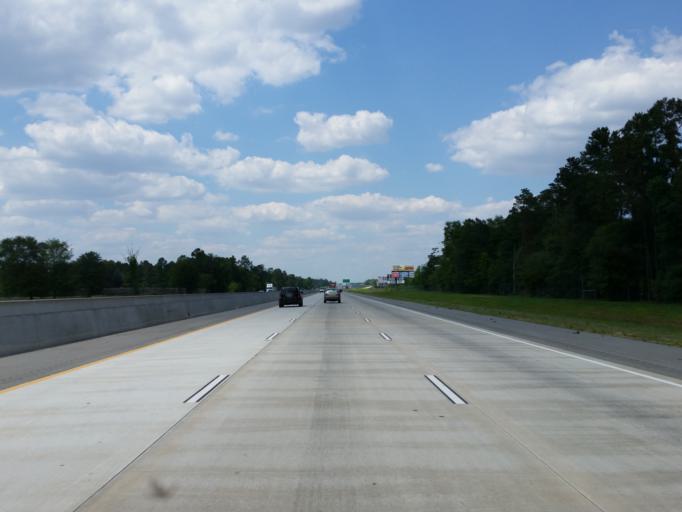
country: US
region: Georgia
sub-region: Cook County
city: Sparks
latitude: 31.1988
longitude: -83.4568
